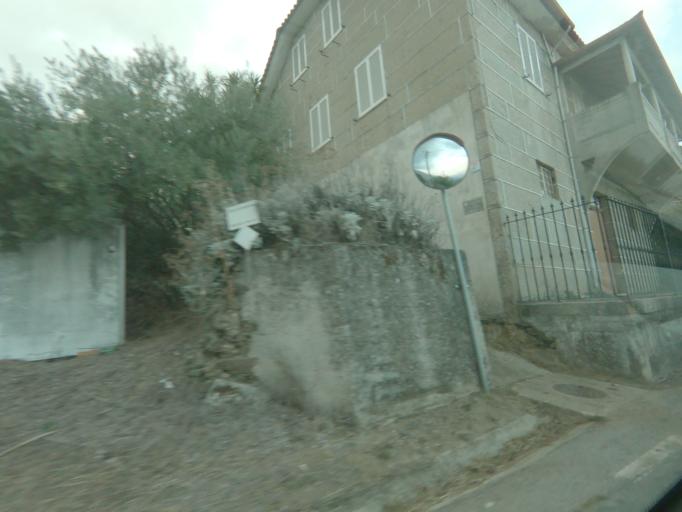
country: PT
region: Vila Real
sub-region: Mesao Frio
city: Mesao Frio
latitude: 41.1700
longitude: -7.8749
